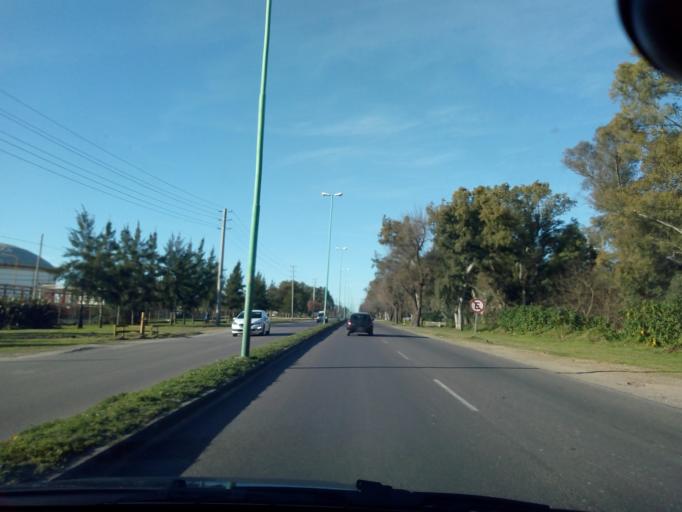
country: AR
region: Buenos Aires
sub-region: Partido de Ensenada
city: Ensenada
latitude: -34.8790
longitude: -57.9215
